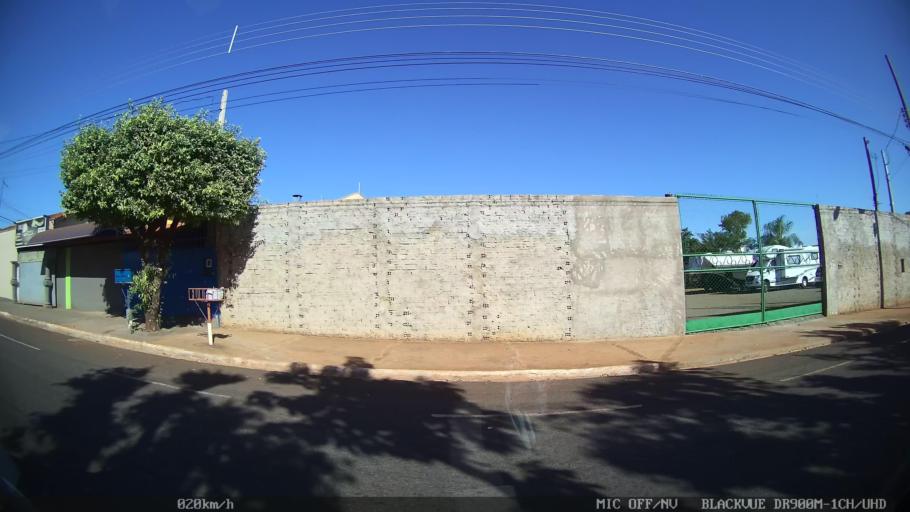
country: BR
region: Sao Paulo
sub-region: Olimpia
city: Olimpia
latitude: -20.7247
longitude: -48.9085
